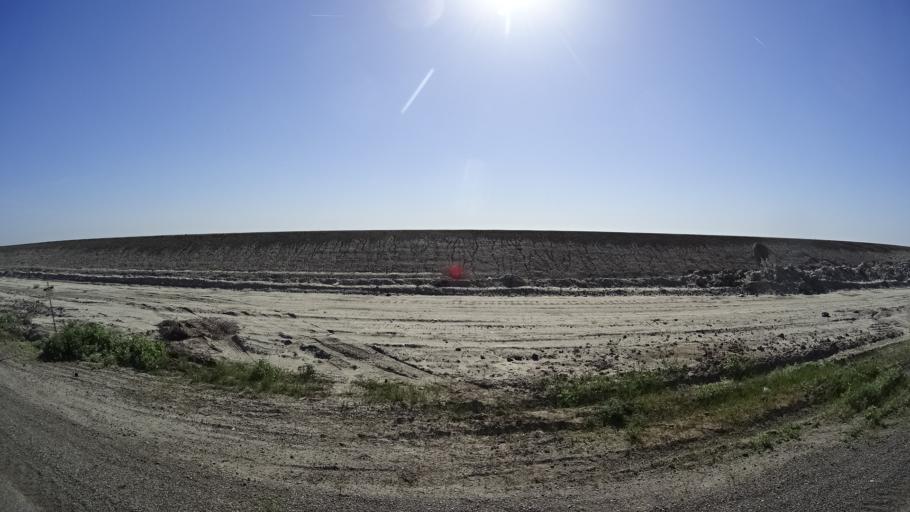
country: US
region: California
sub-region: Kings County
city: Corcoran
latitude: 36.1472
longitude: -119.5649
